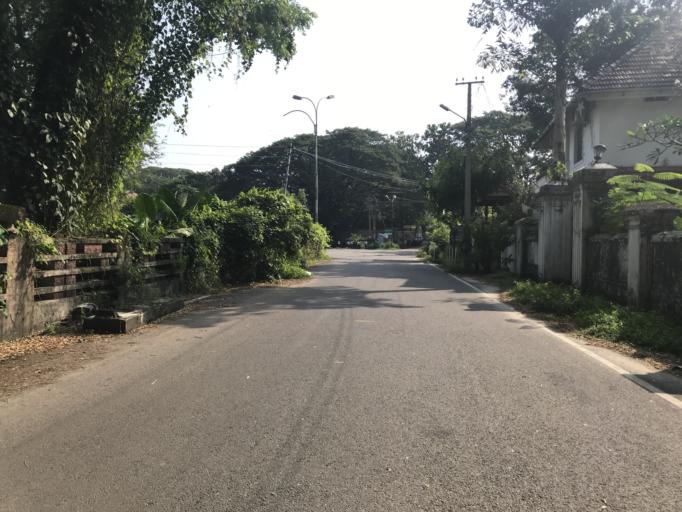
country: IN
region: Kerala
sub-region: Ernakulam
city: Cochin
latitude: 9.9636
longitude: 76.2405
